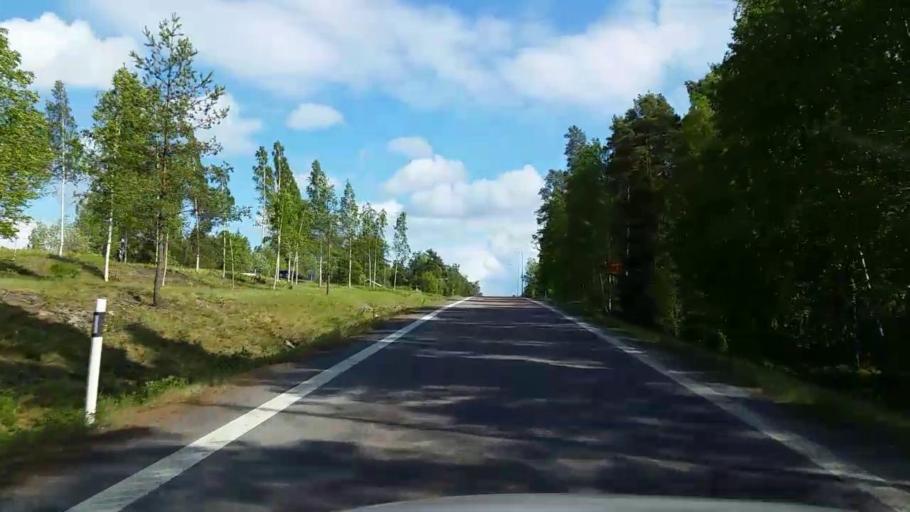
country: SE
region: Dalarna
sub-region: Faluns Kommun
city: Falun
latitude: 60.5934
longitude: 15.6963
